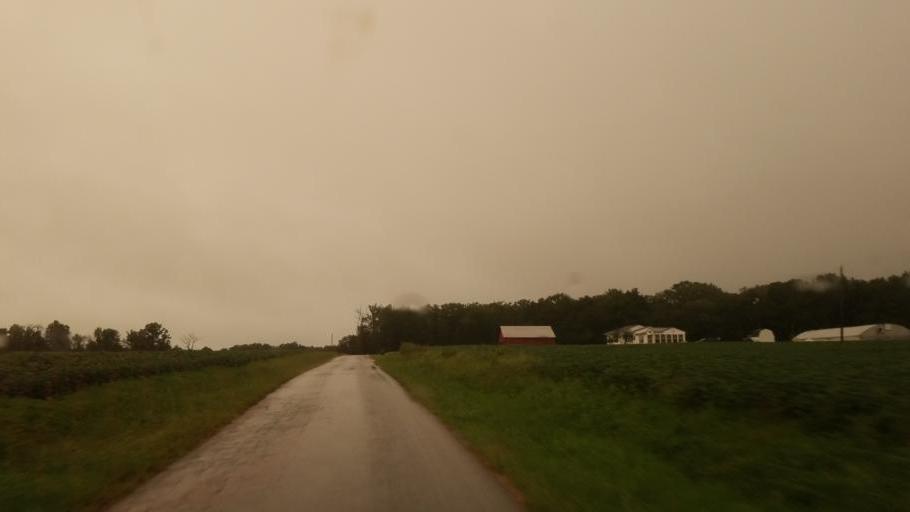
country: US
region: Kentucky
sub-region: Fleming County
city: Flemingsburg
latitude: 38.4653
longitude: -83.6264
